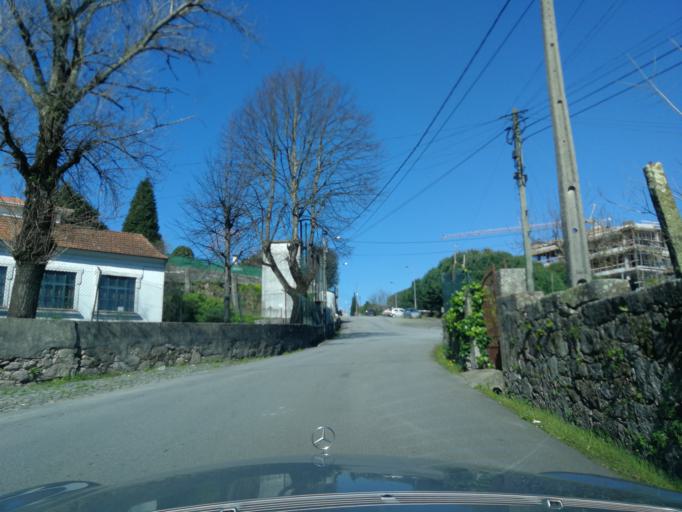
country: PT
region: Braga
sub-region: Vila Nova de Famalicao
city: Calendario
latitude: 41.3971
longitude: -8.5267
